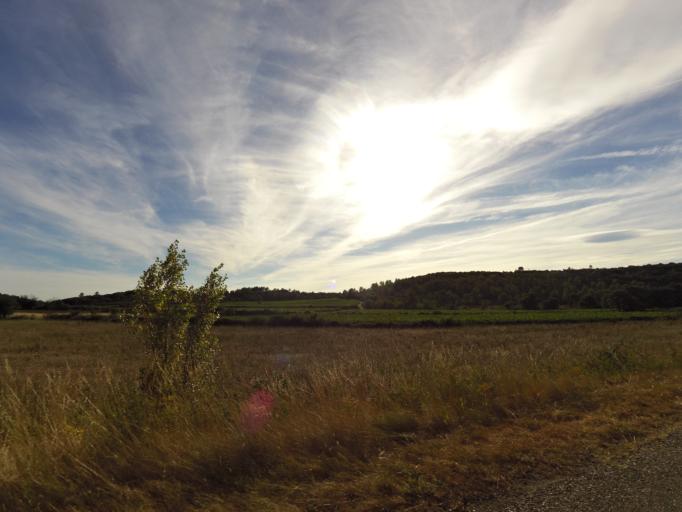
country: FR
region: Languedoc-Roussillon
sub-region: Departement du Gard
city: Congenies
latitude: 43.8088
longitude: 4.1498
